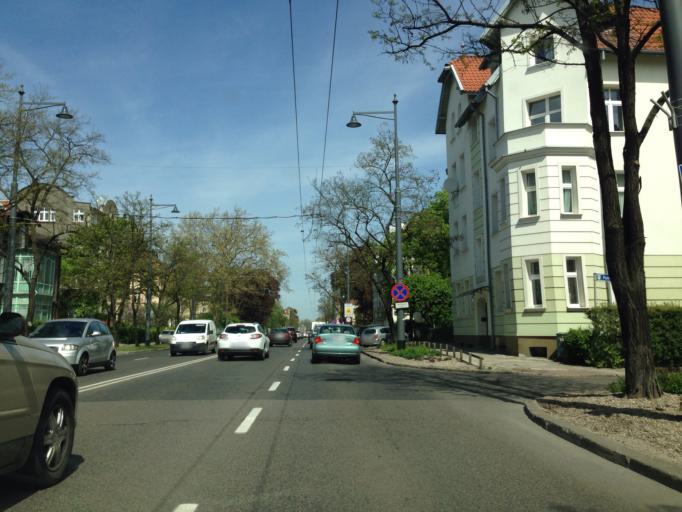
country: PL
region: Pomeranian Voivodeship
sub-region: Sopot
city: Sopot
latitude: 54.4362
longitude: 18.5614
